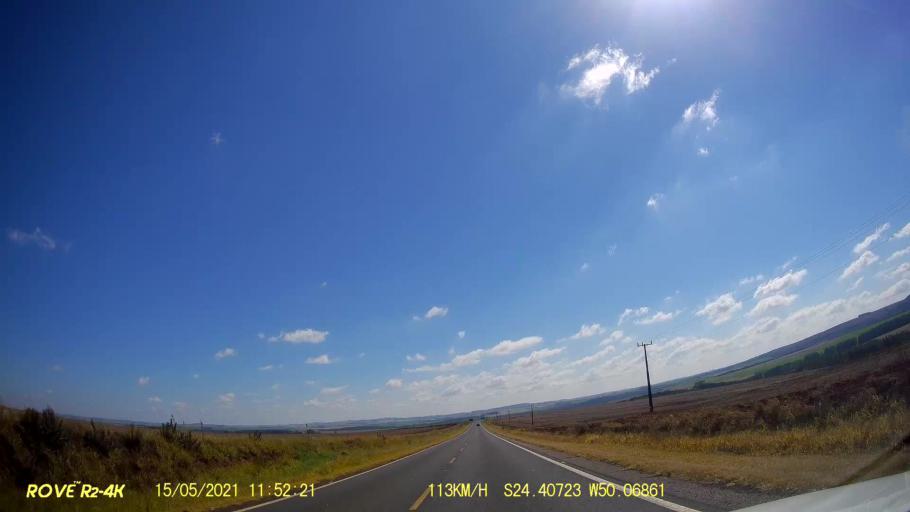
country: BR
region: Parana
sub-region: Pirai Do Sul
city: Pirai do Sul
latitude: -24.4072
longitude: -50.0686
